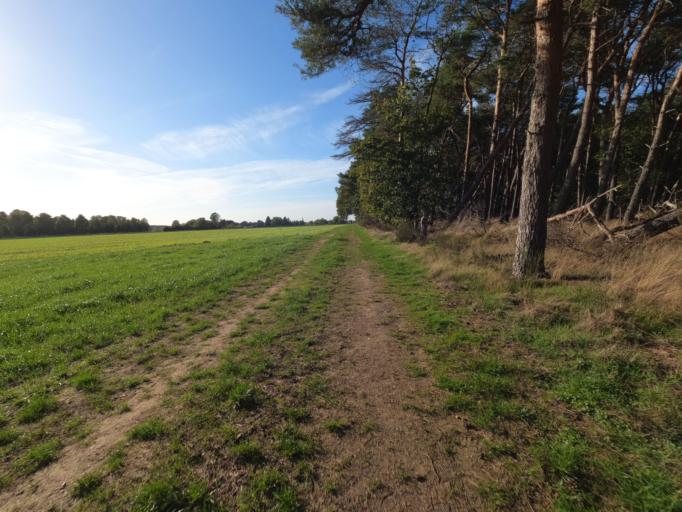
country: DE
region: North Rhine-Westphalia
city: Wegberg
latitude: 51.1390
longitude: 6.2330
